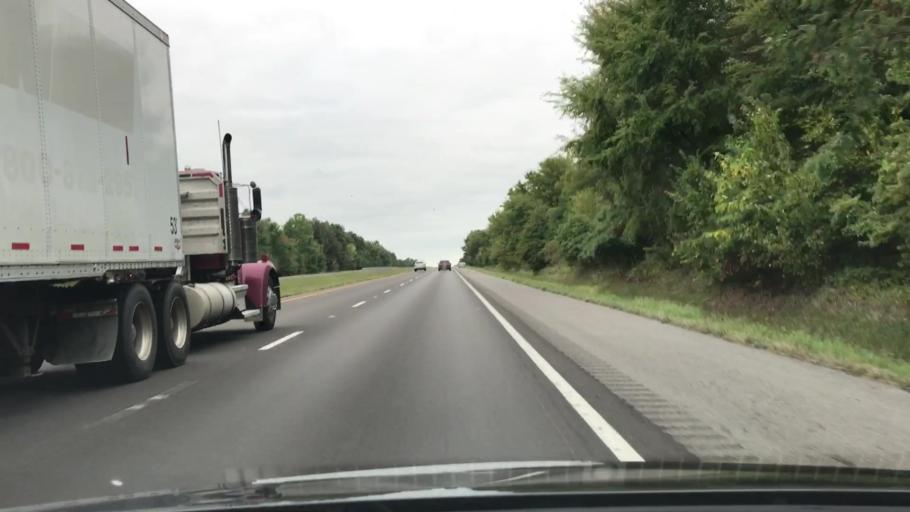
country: US
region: Kentucky
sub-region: Fulton County
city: Fulton
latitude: 36.6309
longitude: -88.7697
